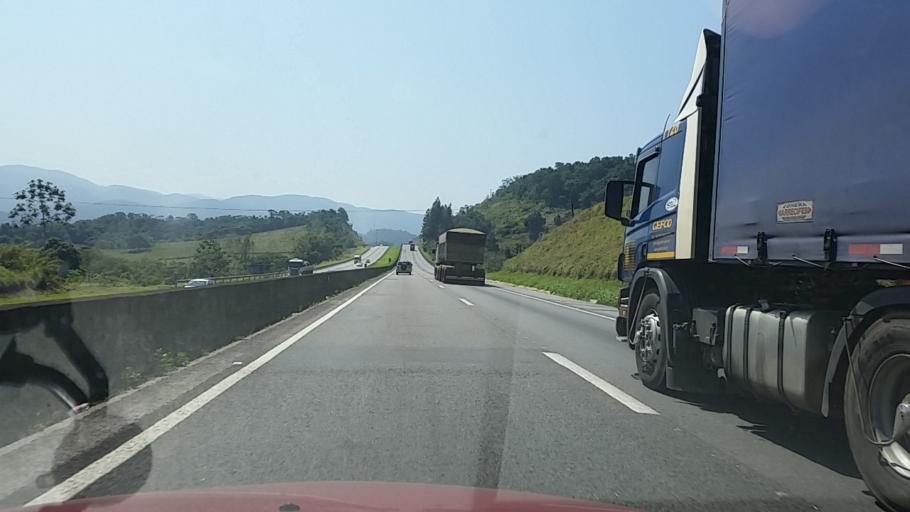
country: BR
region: Sao Paulo
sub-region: Miracatu
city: Miracatu
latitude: -24.1731
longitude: -47.3423
